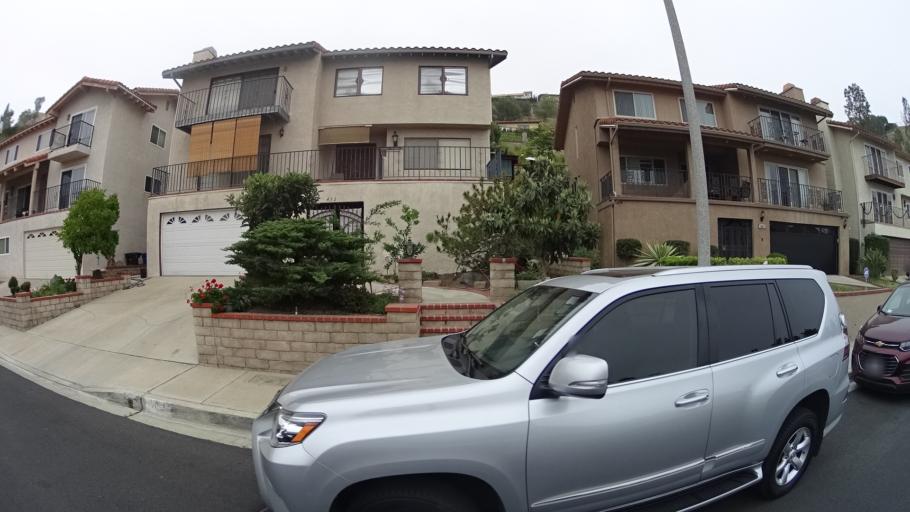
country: US
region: California
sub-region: Los Angeles County
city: Burbank
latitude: 34.1936
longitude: -118.2917
